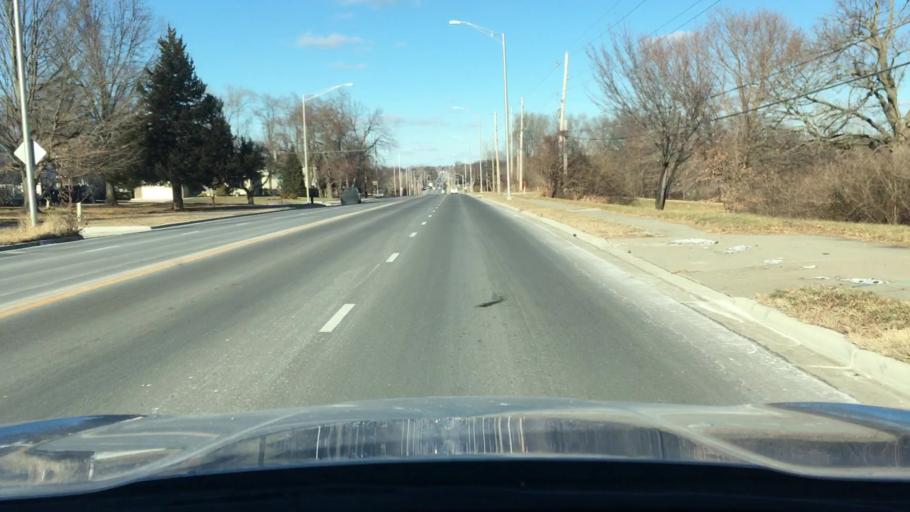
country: US
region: Missouri
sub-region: Jackson County
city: Lees Summit
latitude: 38.8942
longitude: -94.3961
